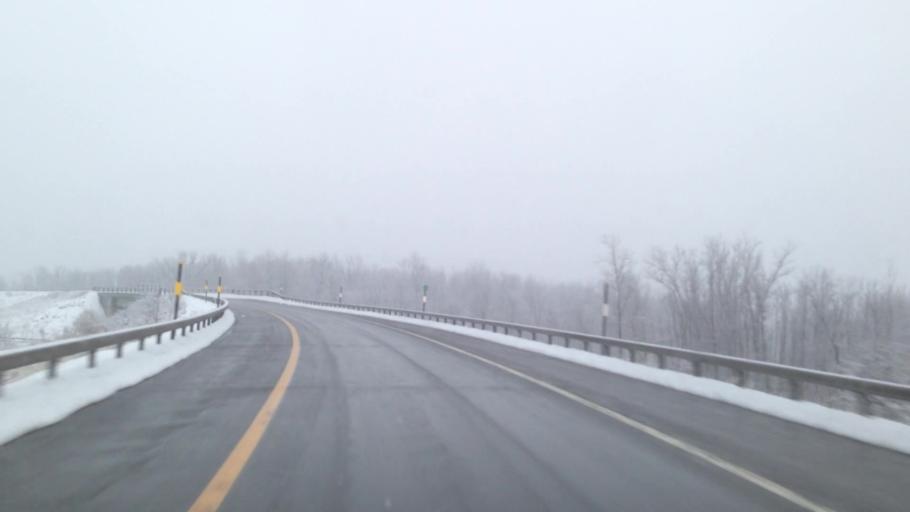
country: US
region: New York
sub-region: Onondaga County
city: East Syracuse
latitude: 43.0544
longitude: -76.0561
